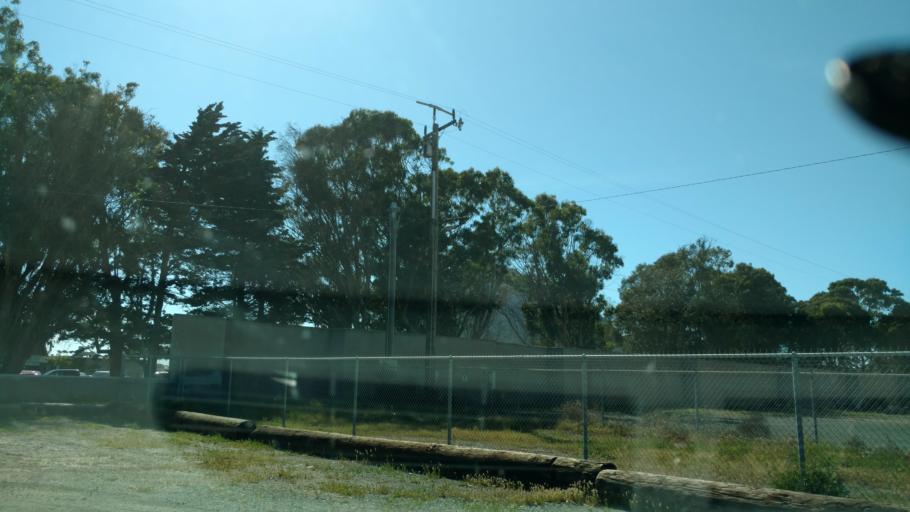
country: US
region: California
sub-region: San Luis Obispo County
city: Morro Bay
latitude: 35.3709
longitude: -120.8559
